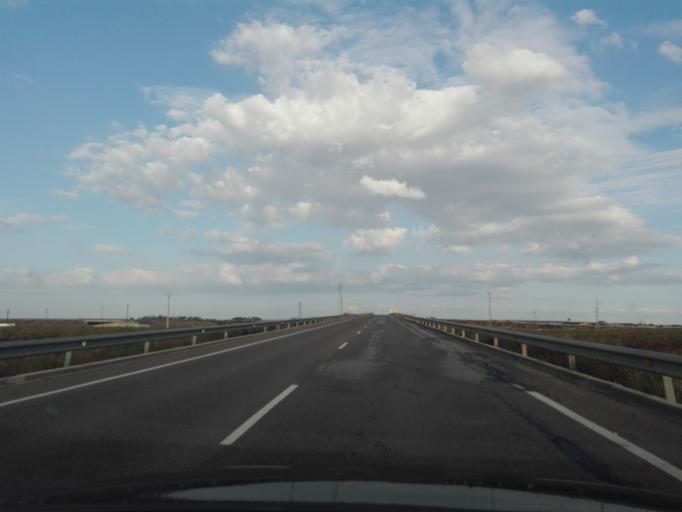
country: ES
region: Extremadura
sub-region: Provincia de Badajoz
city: Almendralejo
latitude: 38.6621
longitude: -6.3864
